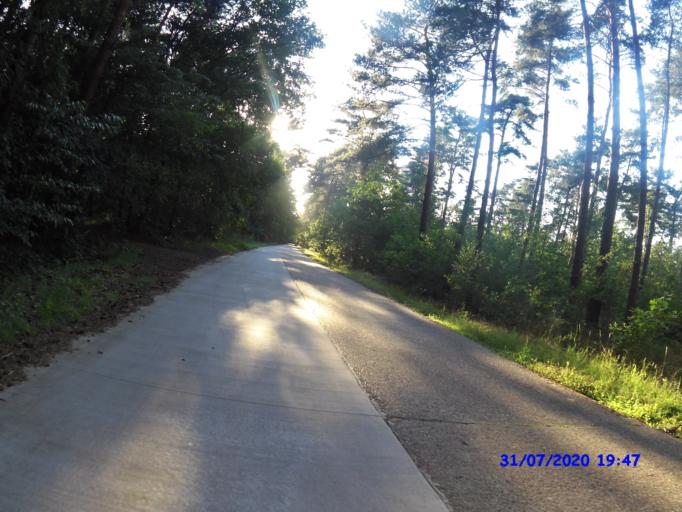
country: BE
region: Flanders
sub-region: Provincie Antwerpen
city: Kasterlee
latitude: 51.2382
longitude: 4.9489
